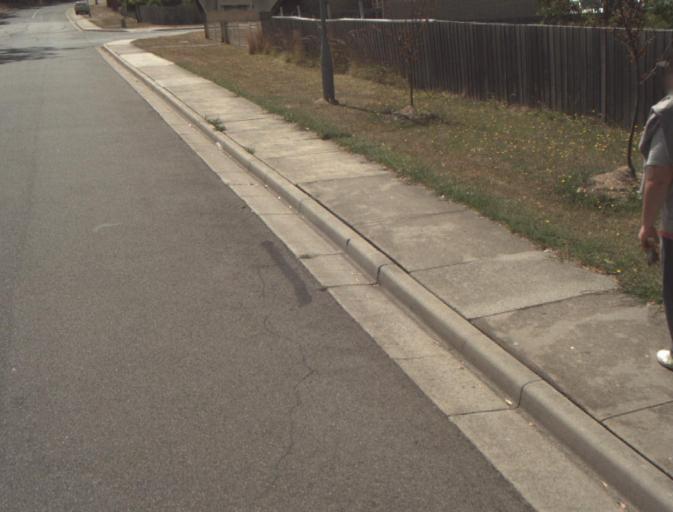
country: AU
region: Tasmania
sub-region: Launceston
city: Newstead
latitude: -41.4161
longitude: 147.1795
